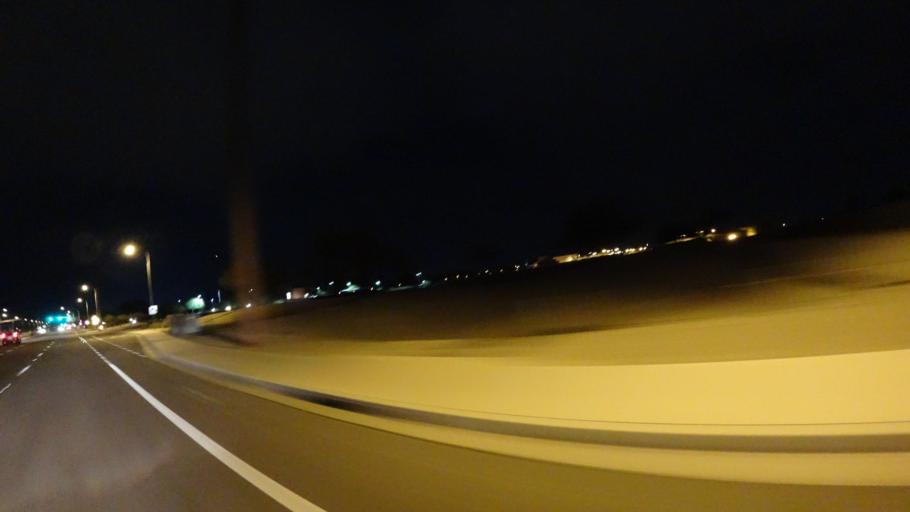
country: US
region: Arizona
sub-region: Maricopa County
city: Chandler
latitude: 33.2917
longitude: -111.8185
